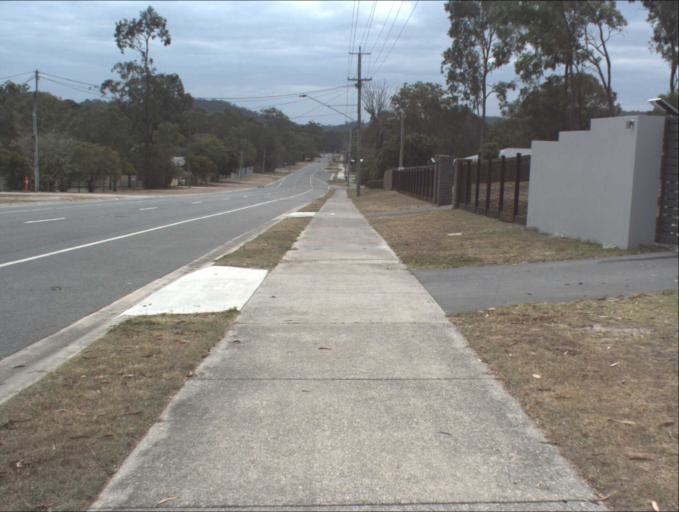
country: AU
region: Queensland
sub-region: Logan
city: Beenleigh
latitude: -27.6671
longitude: 153.2201
